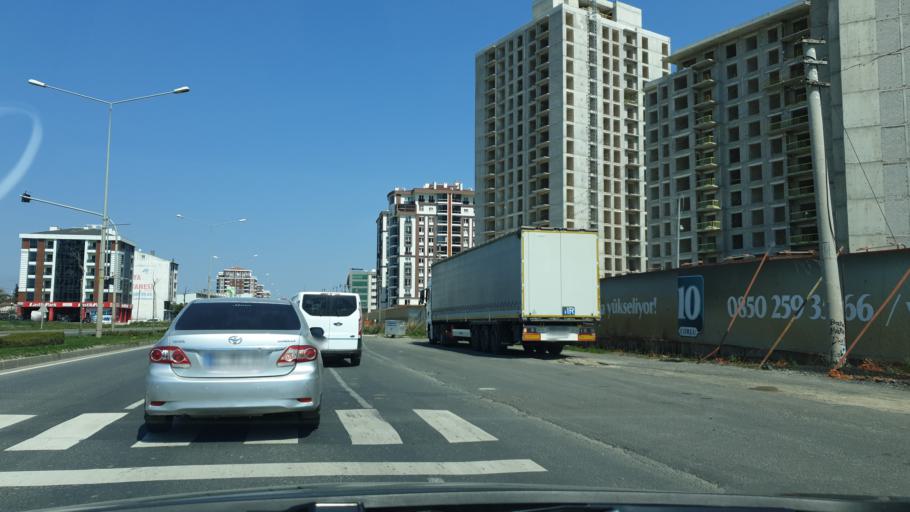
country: TR
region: Tekirdag
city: Corlu
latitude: 41.1505
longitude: 27.7774
